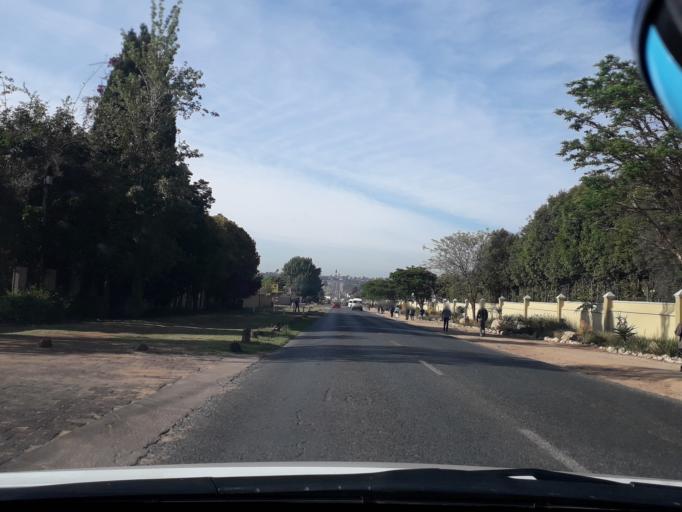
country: ZA
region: Gauteng
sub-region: City of Johannesburg Metropolitan Municipality
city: Roodepoort
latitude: -26.0839
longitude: 27.9273
